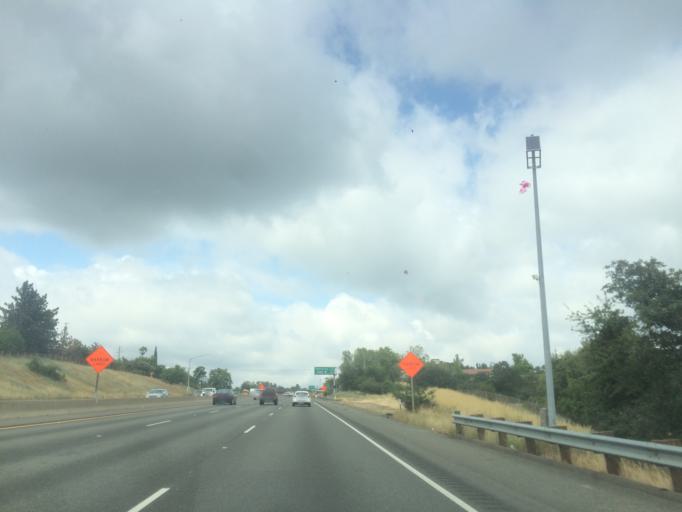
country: US
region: California
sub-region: Placer County
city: Newcastle
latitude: 38.8680
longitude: -121.1323
